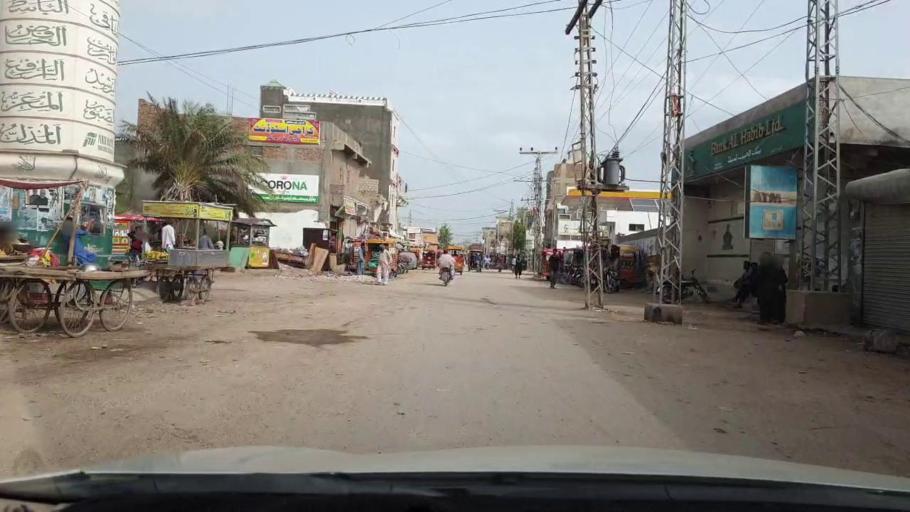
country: PK
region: Sindh
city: Matli
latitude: 25.0434
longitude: 68.6581
